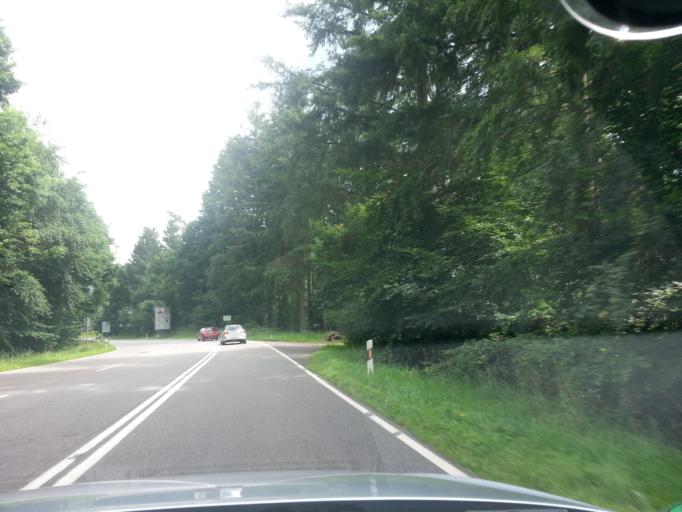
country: DE
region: Saarland
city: Mettlach
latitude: 49.5022
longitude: 6.5827
